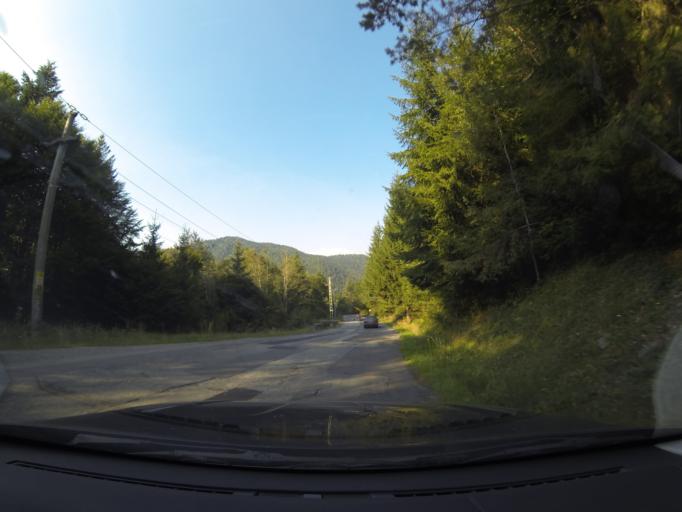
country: RO
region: Arges
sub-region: Comuna Arefu
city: Arefu
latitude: 45.3988
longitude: 24.6386
